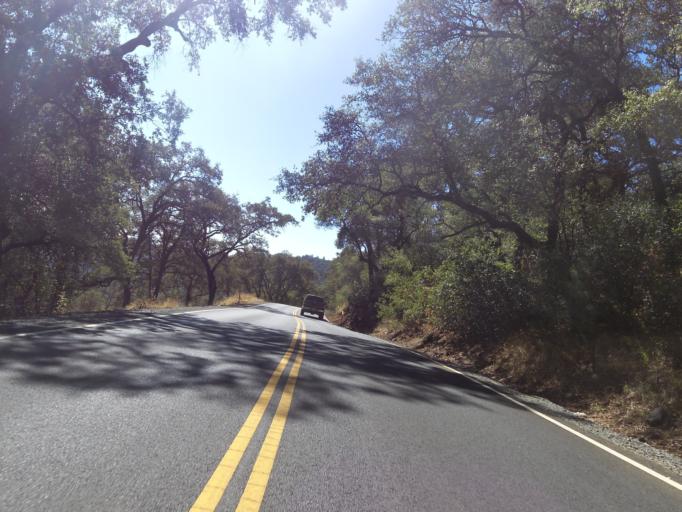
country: US
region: California
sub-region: El Dorado County
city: Deer Park
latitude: 38.6082
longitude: -120.8532
